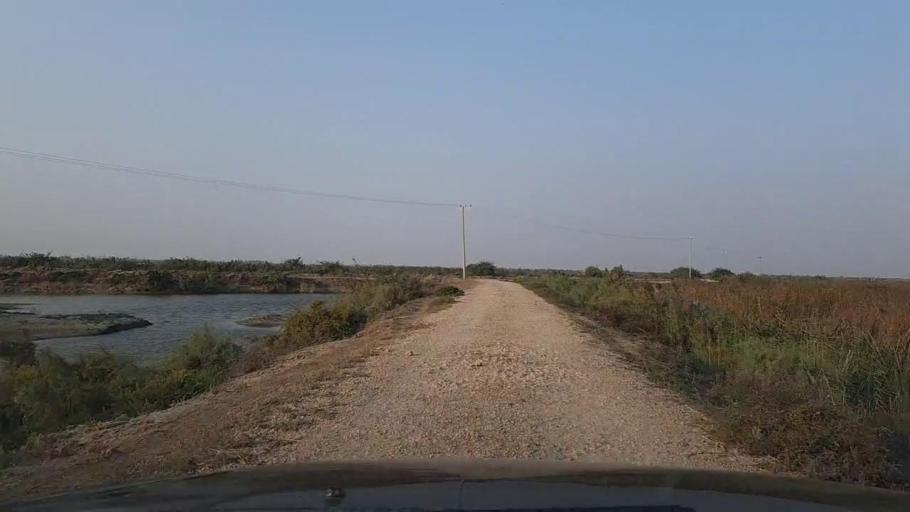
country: PK
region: Sindh
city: Mirpur Sakro
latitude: 24.4144
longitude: 67.7323
